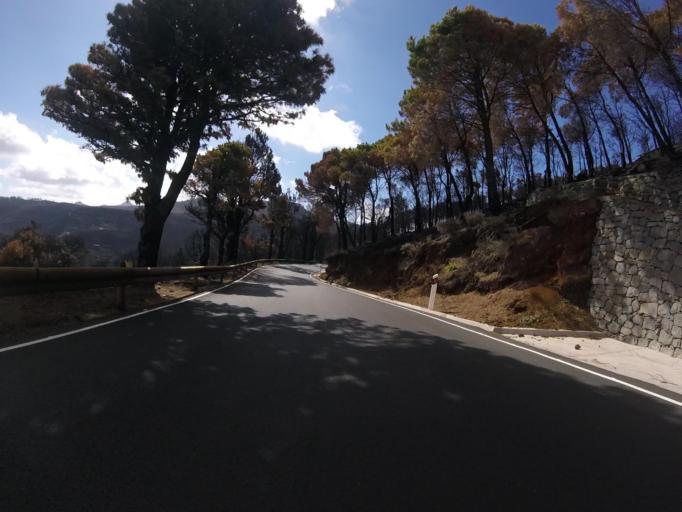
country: ES
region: Canary Islands
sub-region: Provincia de Las Palmas
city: Tejeda
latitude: 27.9948
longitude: -15.5945
